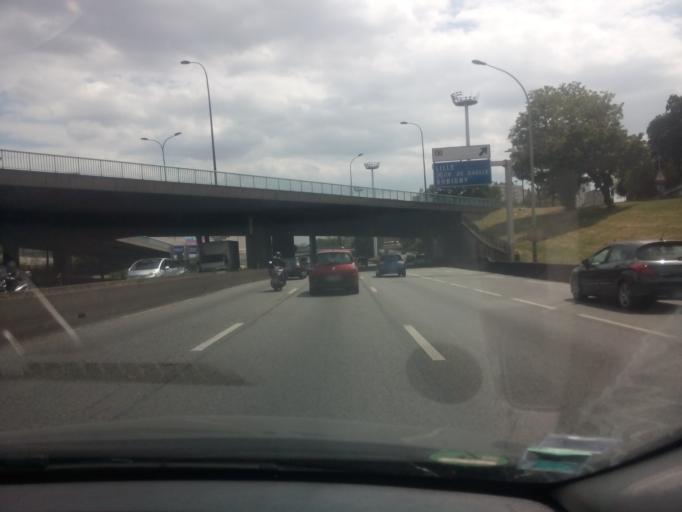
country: FR
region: Ile-de-France
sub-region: Departement de Seine-Saint-Denis
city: Bagnolet
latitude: 48.8677
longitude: 2.4134
